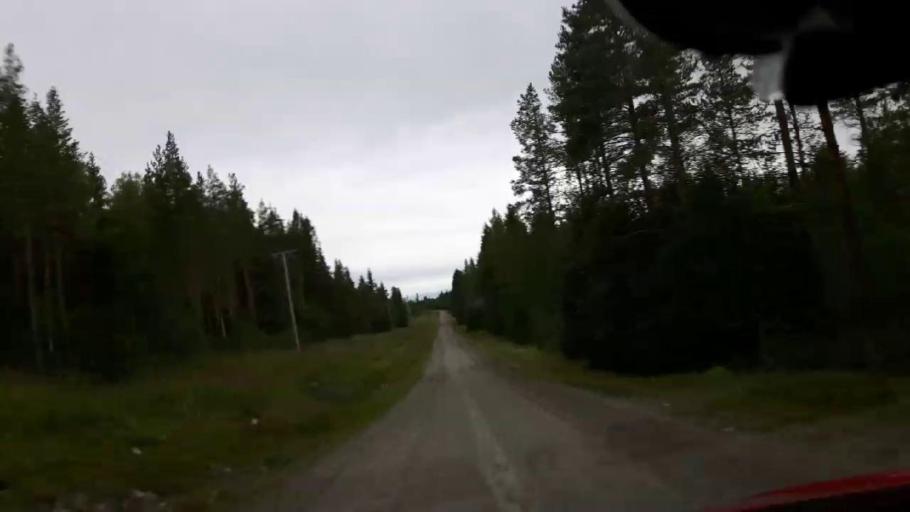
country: SE
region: Vaesternorrland
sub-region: Ange Kommun
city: Ange
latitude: 62.8532
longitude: 15.9215
